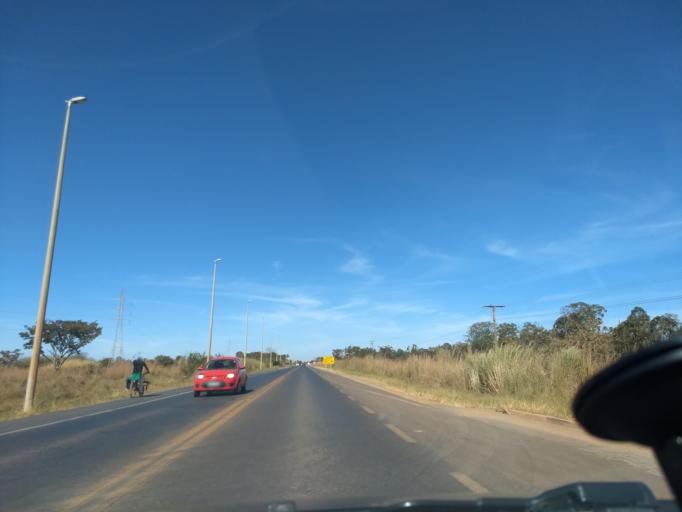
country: BR
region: Federal District
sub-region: Brasilia
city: Brasilia
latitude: -15.7788
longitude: -48.0477
